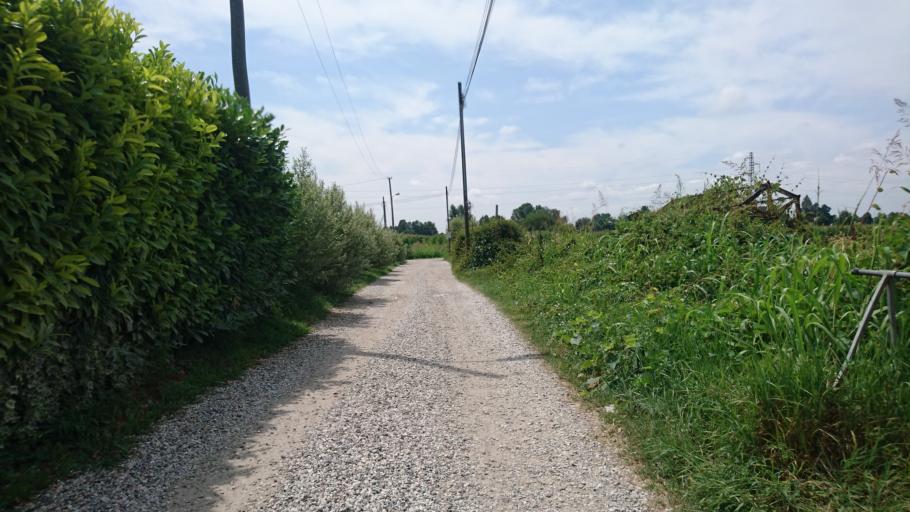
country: IT
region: Veneto
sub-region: Provincia di Padova
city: Sarmeola
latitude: 45.4210
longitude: 11.8467
